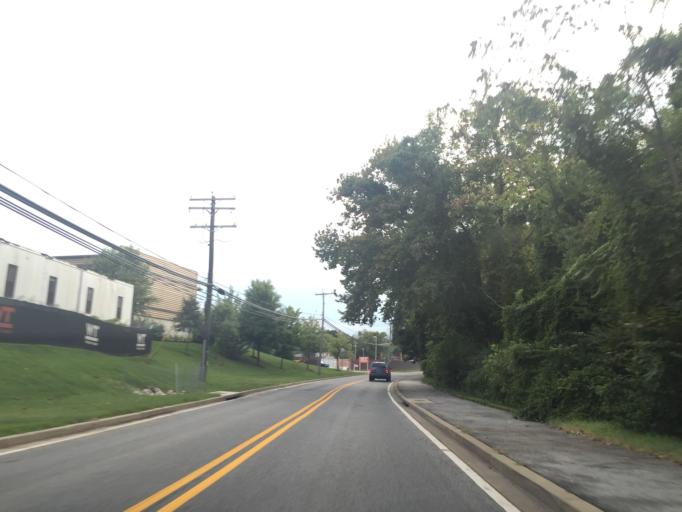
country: US
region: Maryland
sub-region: Anne Arundel County
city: Brooklyn Park
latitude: 39.2235
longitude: -76.6260
